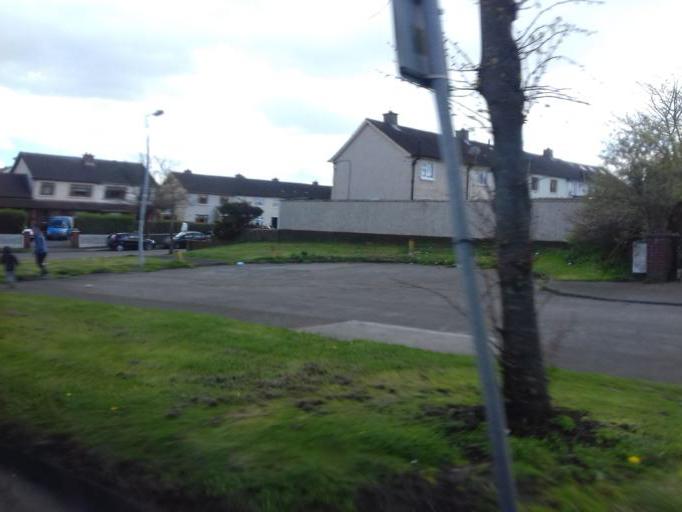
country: IE
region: Leinster
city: Donaghmede
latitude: 53.3909
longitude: -6.1612
